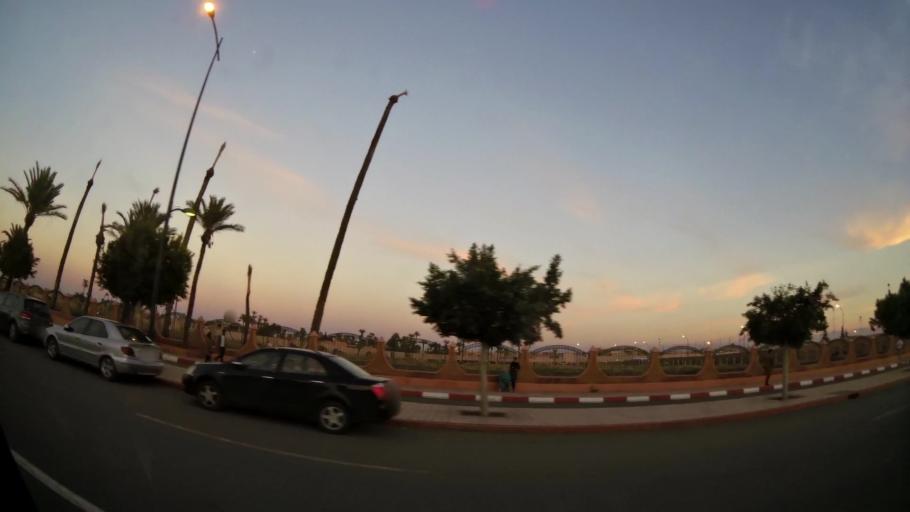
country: MA
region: Marrakech-Tensift-Al Haouz
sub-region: Marrakech
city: Marrakesh
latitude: 31.6407
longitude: -7.9968
